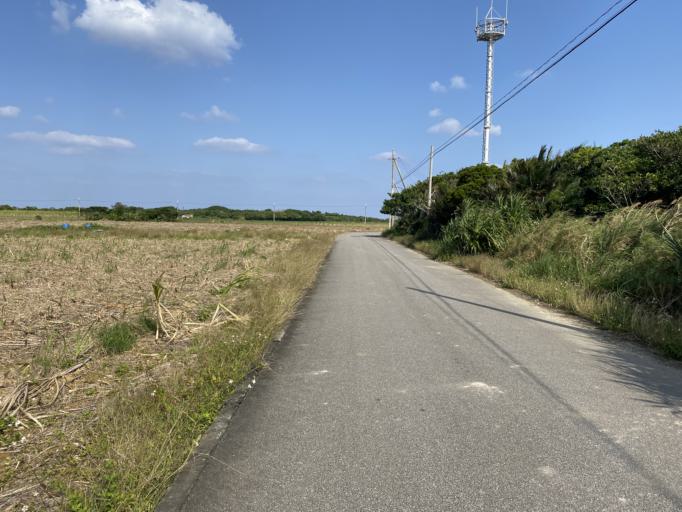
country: JP
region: Okinawa
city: Ishigaki
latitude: 24.0586
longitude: 123.7827
